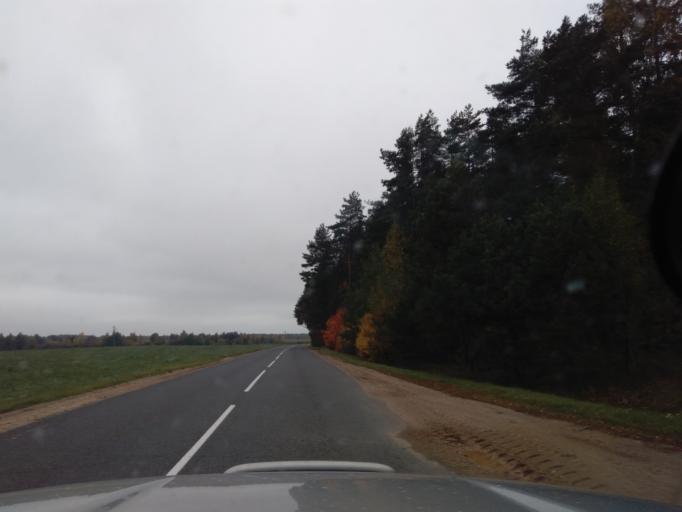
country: BY
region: Minsk
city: Kapyl'
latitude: 53.1528
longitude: 27.2197
